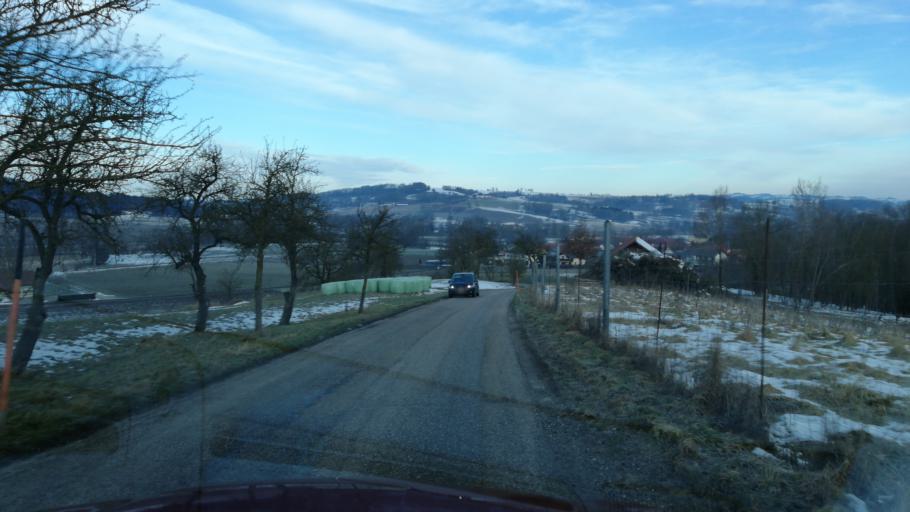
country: AT
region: Upper Austria
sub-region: Wels-Land
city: Buchkirchen
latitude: 48.2438
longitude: 13.9809
